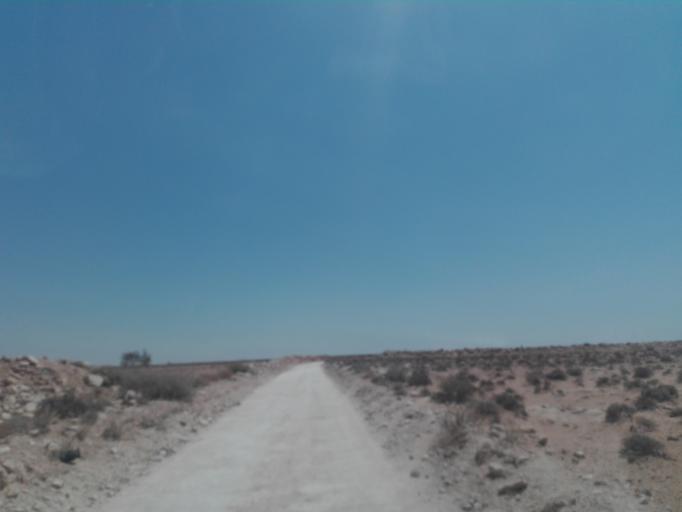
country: TN
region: Safaqis
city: Skhira
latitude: 34.4180
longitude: 9.9522
